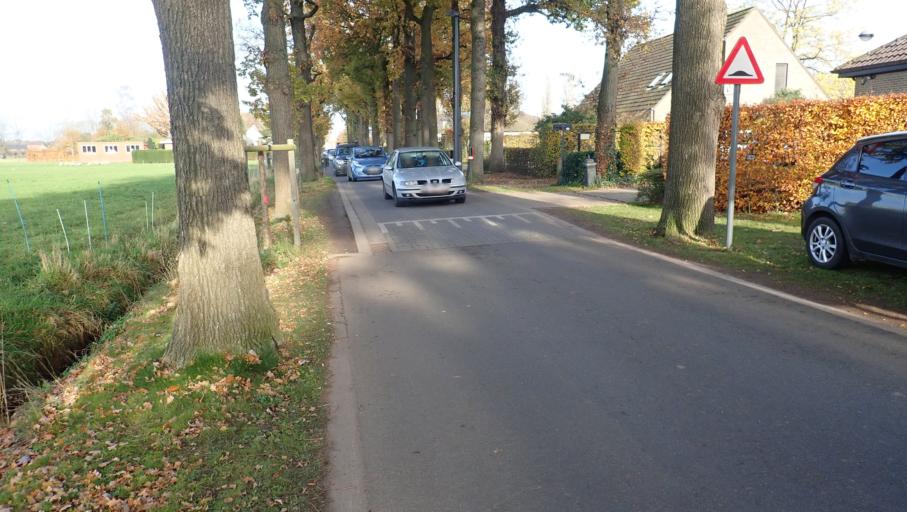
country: BE
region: Flanders
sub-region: Provincie Antwerpen
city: Kalmthout
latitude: 51.3520
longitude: 4.5336
